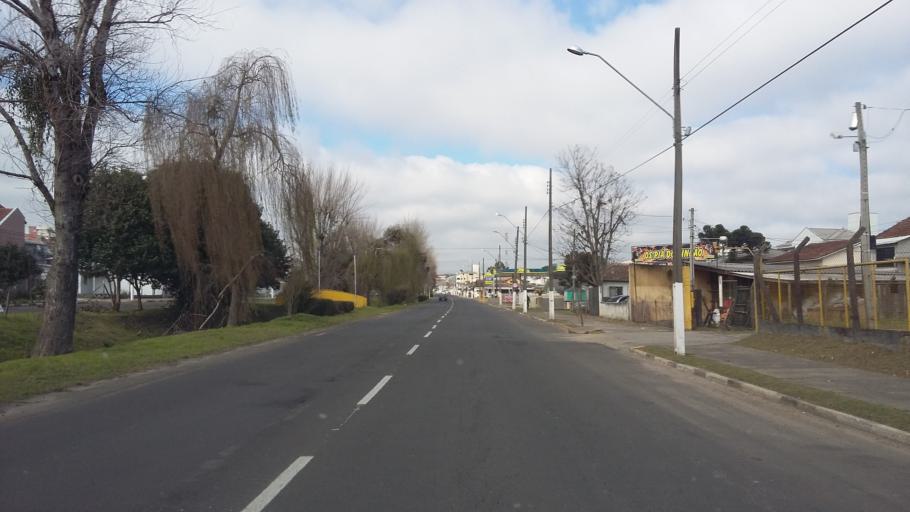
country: BR
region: Santa Catarina
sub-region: Lages
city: Lages
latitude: -27.8171
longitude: -50.3387
